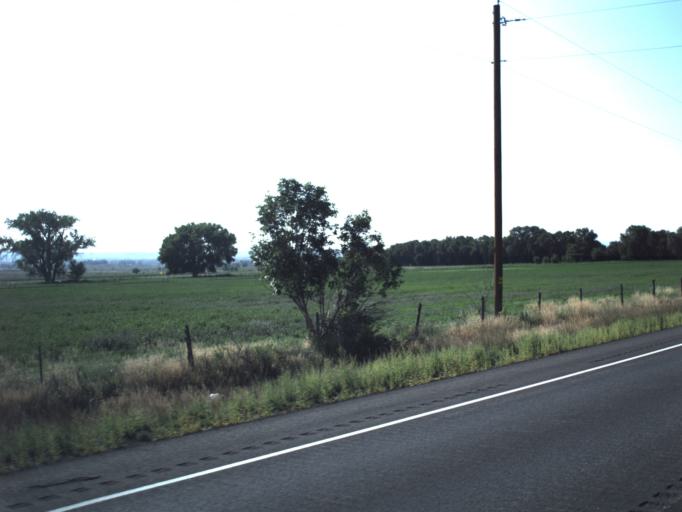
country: US
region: Utah
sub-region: Emery County
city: Huntington
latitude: 39.3084
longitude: -110.9643
